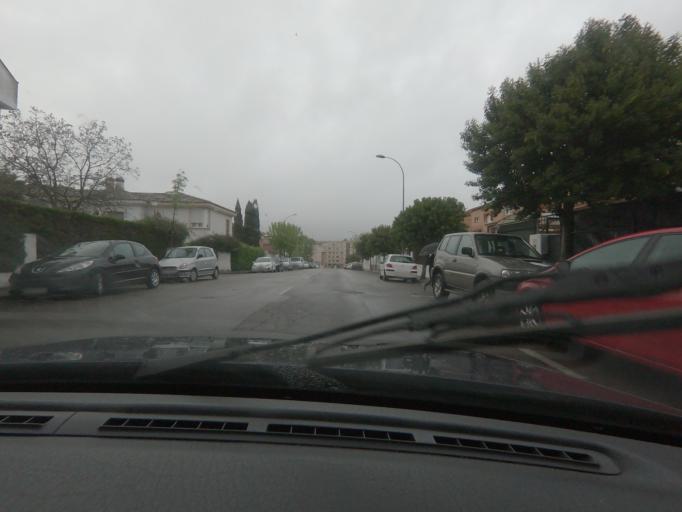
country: ES
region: Extremadura
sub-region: Provincia de Badajoz
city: Merida
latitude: 38.9098
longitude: -6.3627
